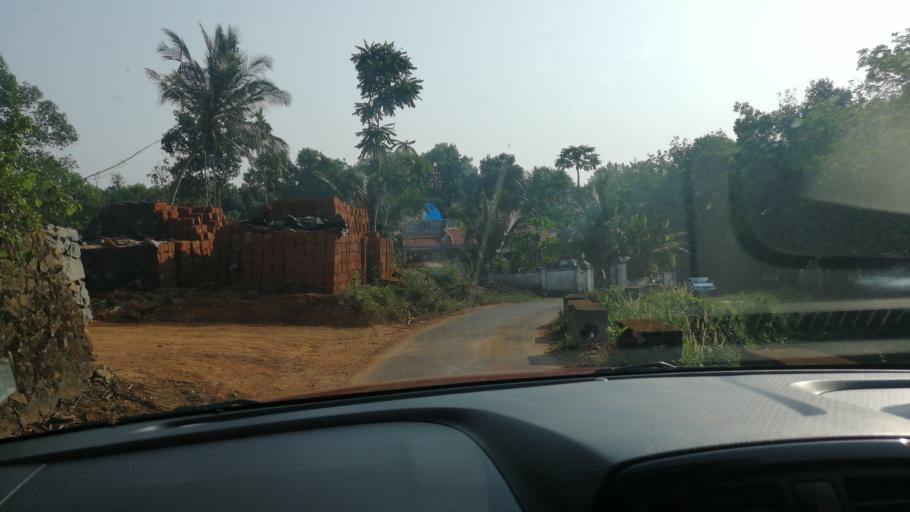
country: IN
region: Kerala
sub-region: Ernakulam
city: Piravam
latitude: 9.8952
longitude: 76.4449
